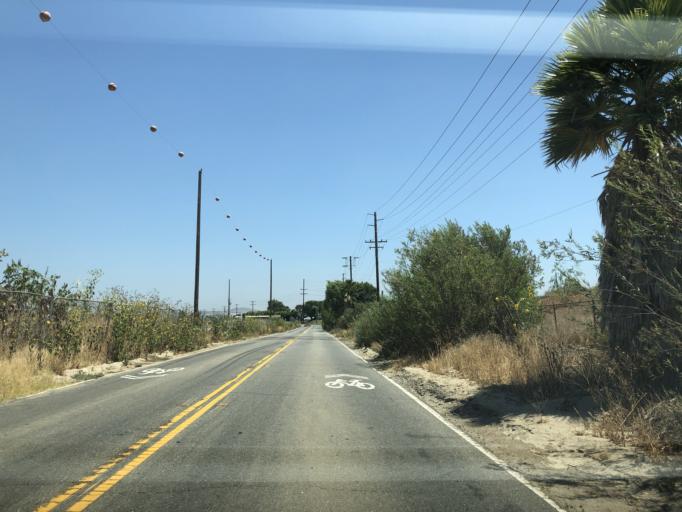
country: US
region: California
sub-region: Riverside County
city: Corona
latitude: 33.8980
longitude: -117.5916
